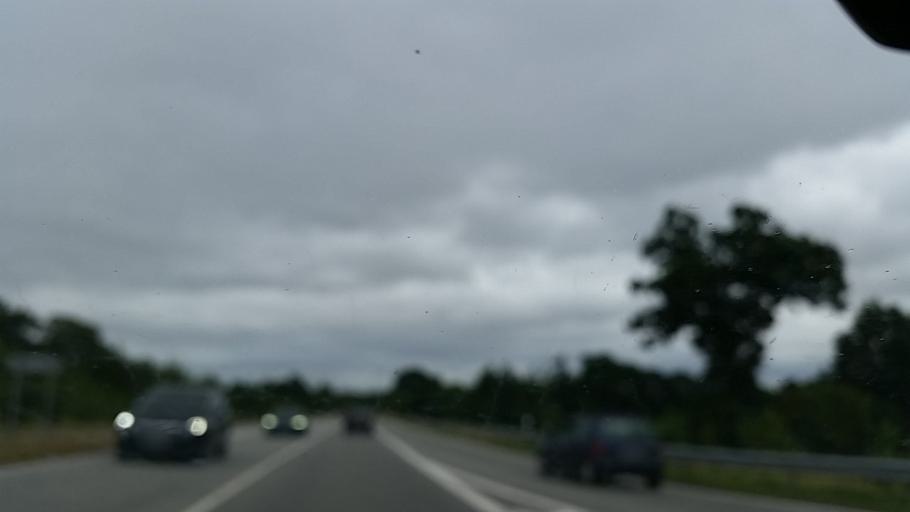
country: DE
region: Schleswig-Holstein
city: Gettorf
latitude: 54.4139
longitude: 9.9912
